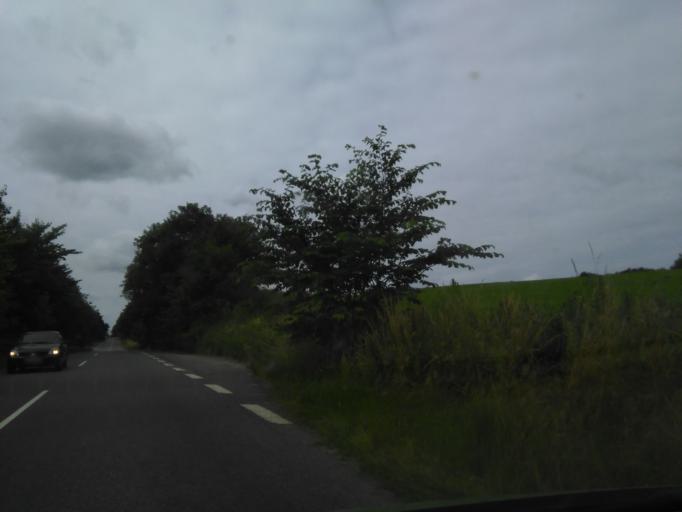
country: DK
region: Central Jutland
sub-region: Arhus Kommune
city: Solbjerg
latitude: 56.0339
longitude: 10.0723
